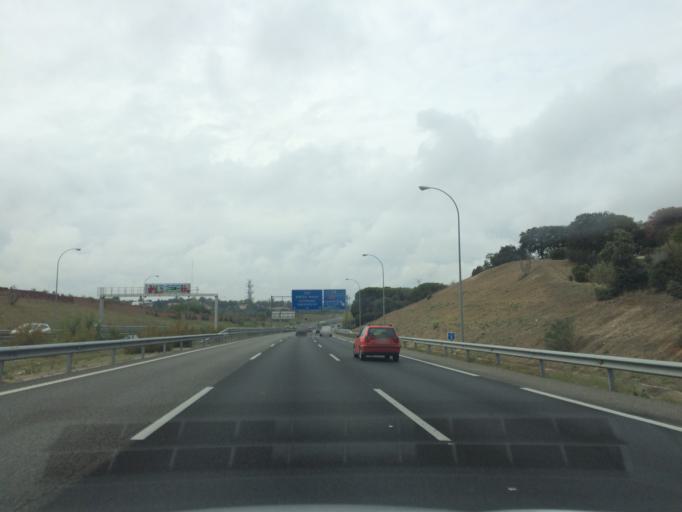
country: ES
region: Madrid
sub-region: Provincia de Madrid
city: Pozuelo de Alarcon
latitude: 40.4512
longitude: -3.8195
